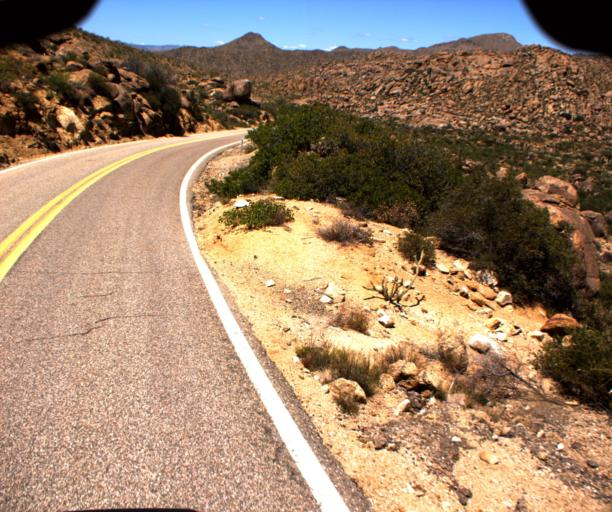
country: US
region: Arizona
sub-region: Yavapai County
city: Bagdad
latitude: 34.4512
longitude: -112.9762
